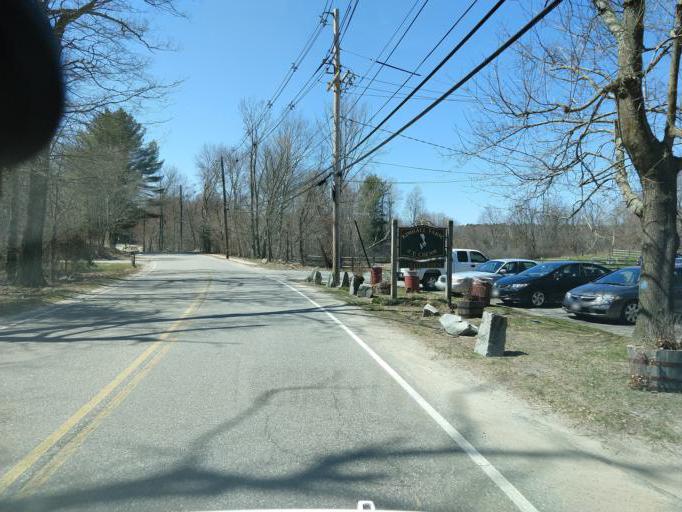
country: US
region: Massachusetts
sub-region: Middlesex County
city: Carlisle
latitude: 42.5249
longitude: -71.3386
